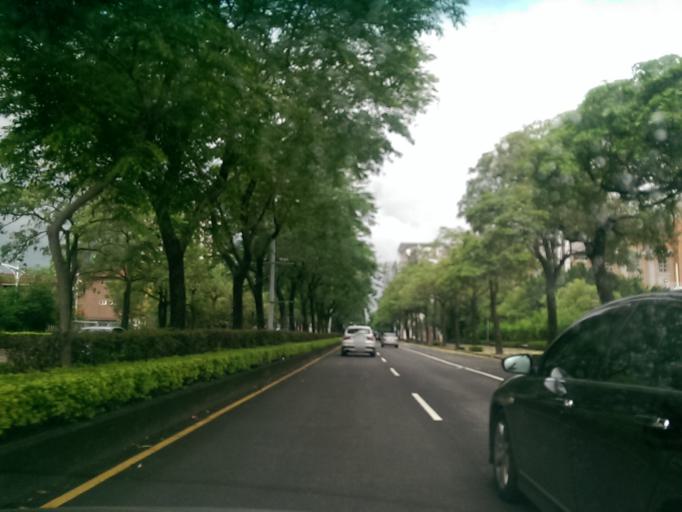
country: TW
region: Taiwan
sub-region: Taichung City
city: Taichung
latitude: 24.1533
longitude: 120.6407
